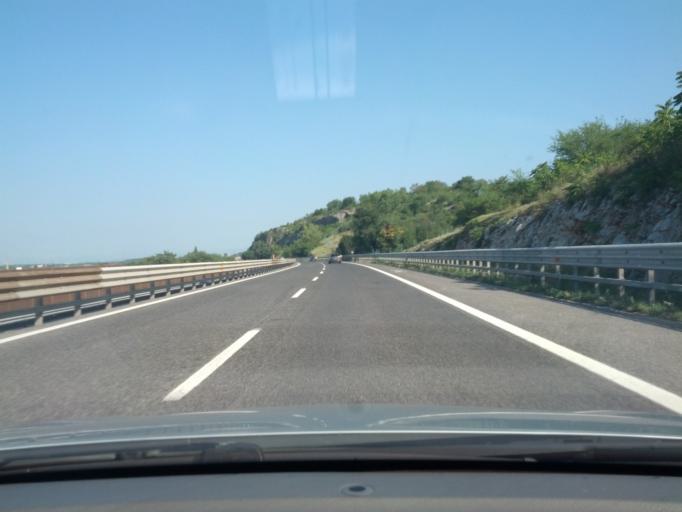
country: IT
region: Friuli Venezia Giulia
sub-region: Provincia di Gorizia
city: Ronchi dei Legionari
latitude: 45.8253
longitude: 13.5245
